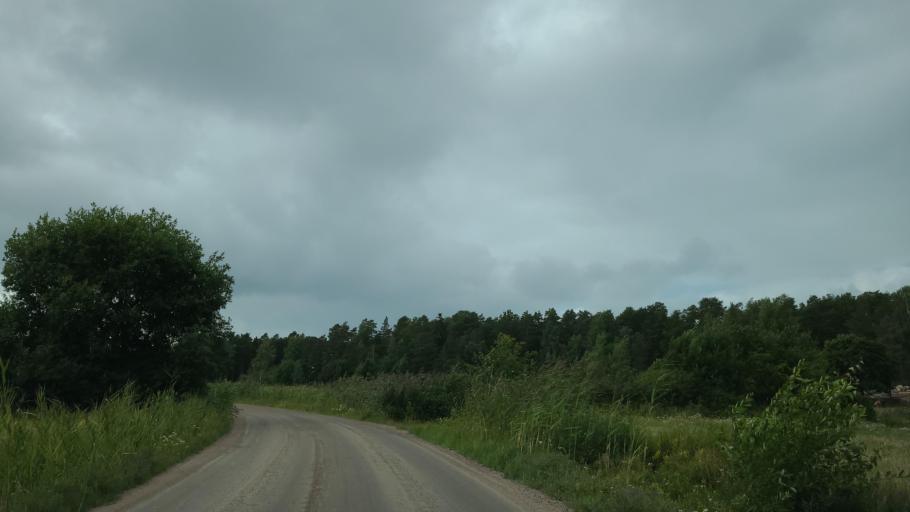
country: FI
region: Varsinais-Suomi
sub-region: Aboland-Turunmaa
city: Nagu
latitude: 60.2030
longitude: 21.8741
